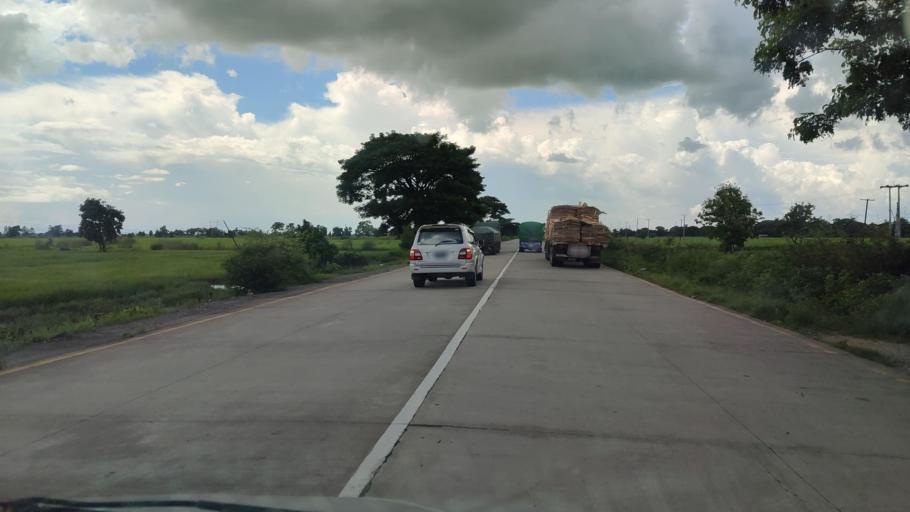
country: MM
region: Bago
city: Nyaunglebin
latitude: 17.9858
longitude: 96.7084
